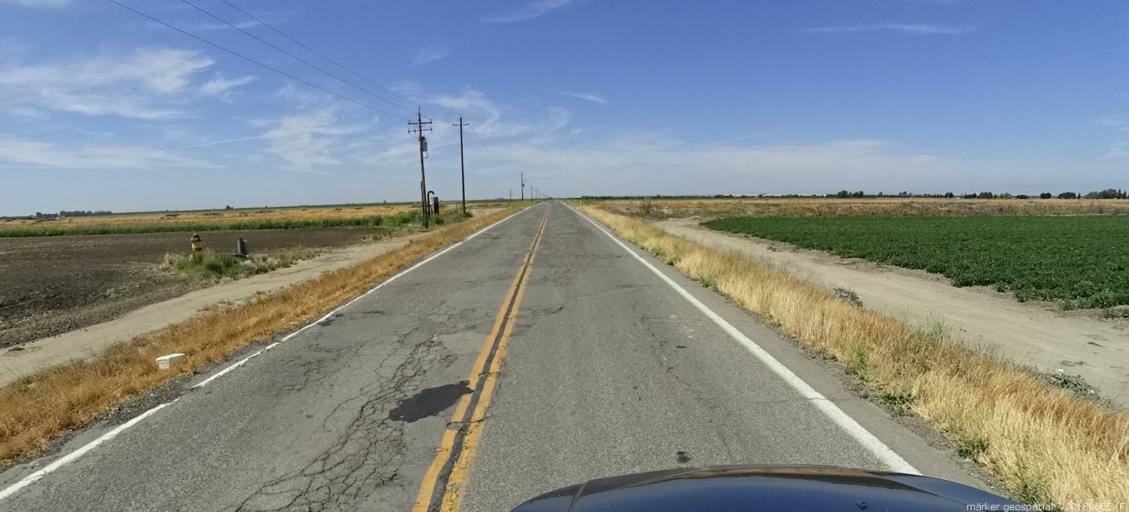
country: US
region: California
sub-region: Fresno County
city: Firebaugh
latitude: 36.9946
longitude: -120.3832
